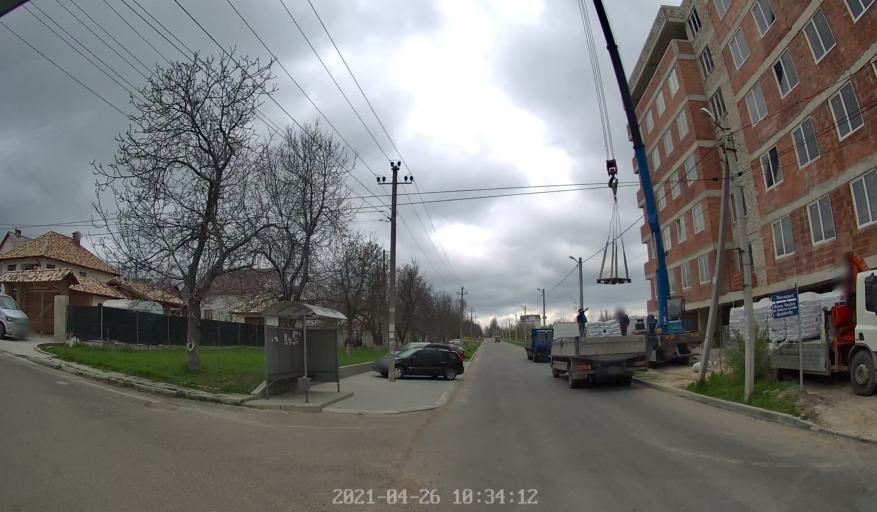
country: MD
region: Chisinau
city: Cricova
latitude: 47.1313
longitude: 28.8615
